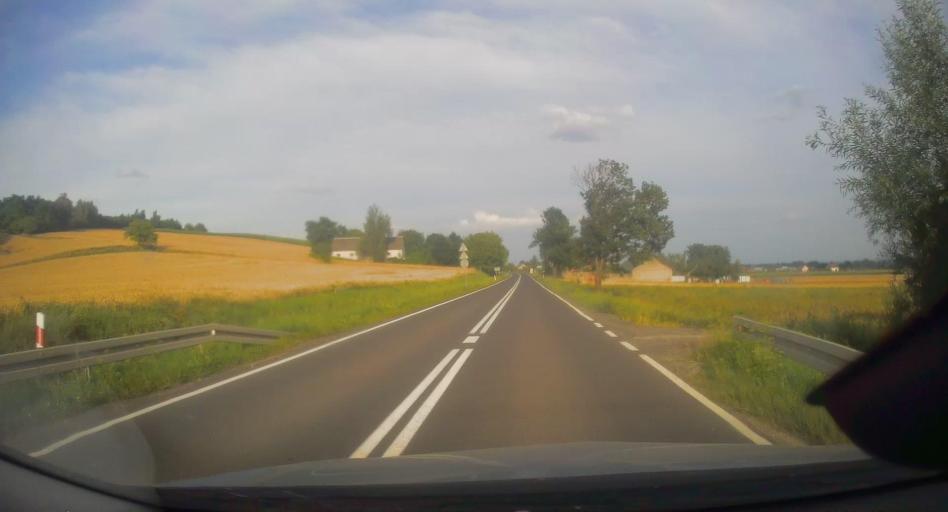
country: PL
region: Lesser Poland Voivodeship
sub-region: Powiat bochenski
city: Dziewin
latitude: 50.1429
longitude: 20.4820
